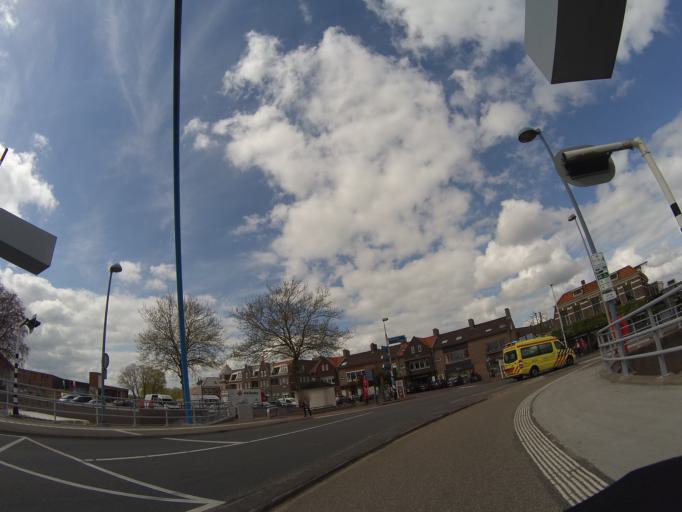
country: NL
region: Overijssel
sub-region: Gemeente Dalfsen
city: Dalfsen
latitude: 52.5028
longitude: 6.2599
